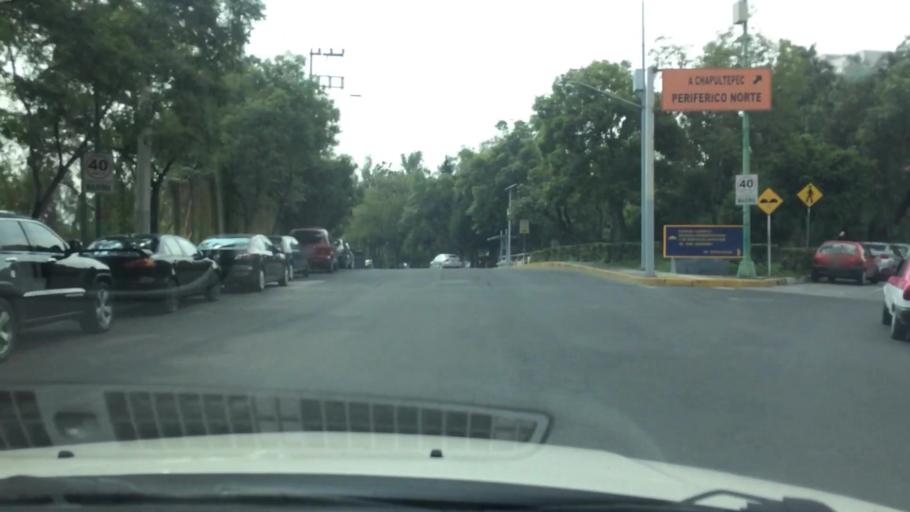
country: MX
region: Mexico City
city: Magdalena Contreras
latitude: 19.3350
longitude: -99.1923
